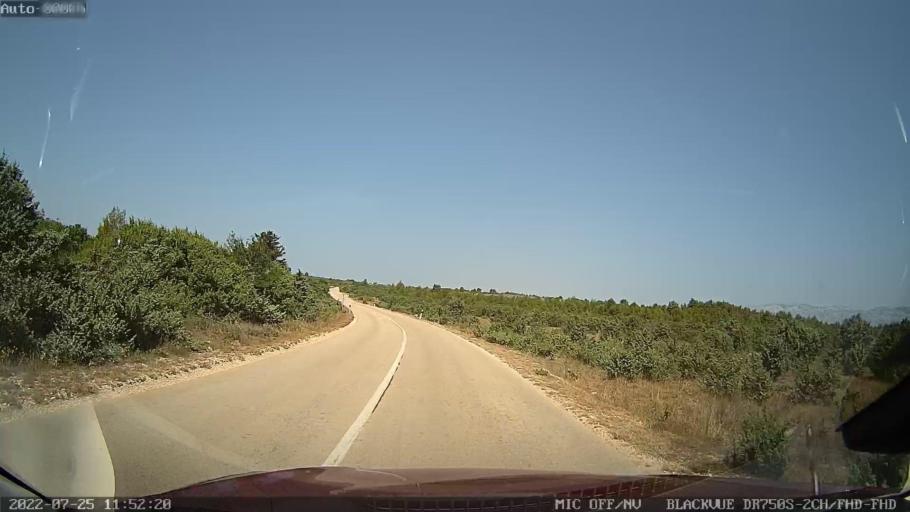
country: HR
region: Zadarska
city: Vrsi
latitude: 44.2472
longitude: 15.2453
